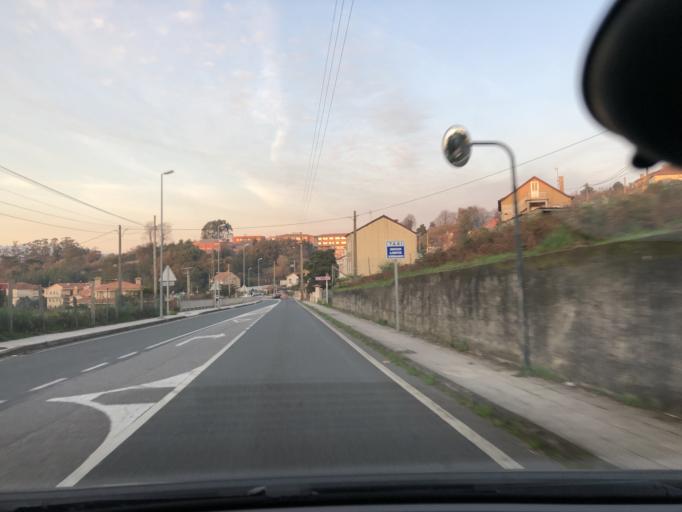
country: ES
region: Galicia
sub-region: Provincia de Pontevedra
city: Marin
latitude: 42.3865
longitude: -8.7127
